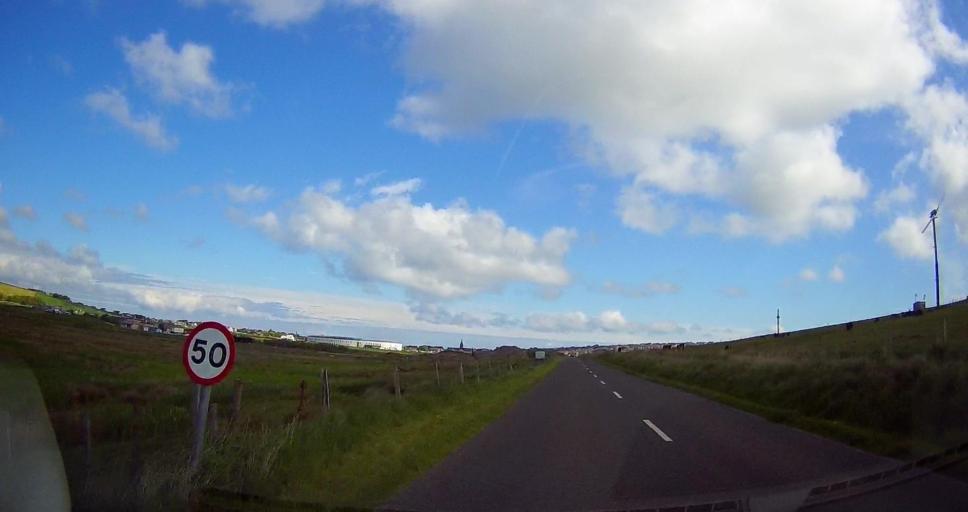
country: GB
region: Scotland
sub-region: Orkney Islands
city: Orkney
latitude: 58.9656
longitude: -2.9657
